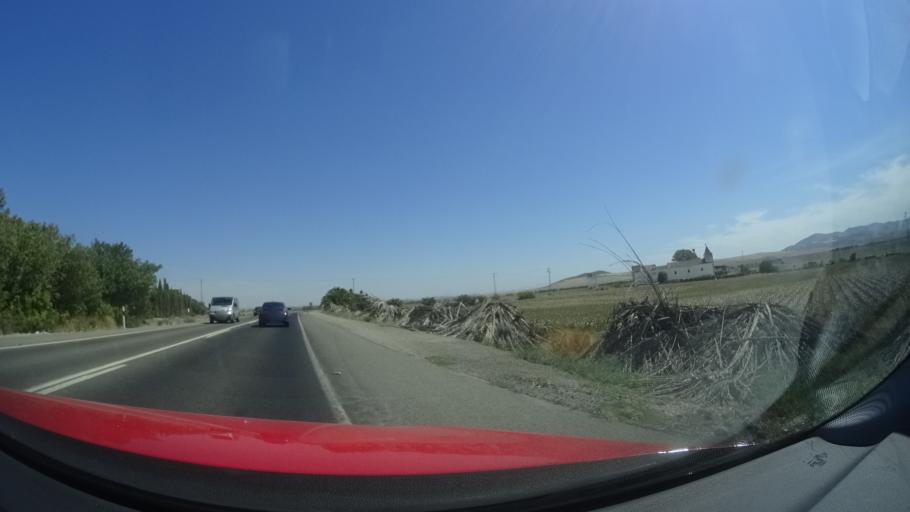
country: ES
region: Andalusia
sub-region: Provincia de Sevilla
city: Lebrija
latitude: 36.8961
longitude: -5.9970
